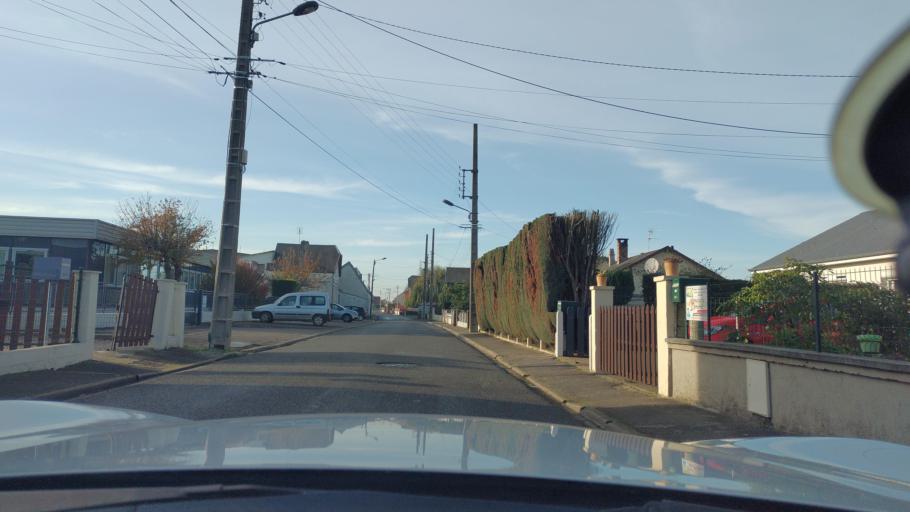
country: FR
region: Picardie
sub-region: Departement de la Somme
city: Fressenneville
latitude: 50.0638
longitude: 1.5771
